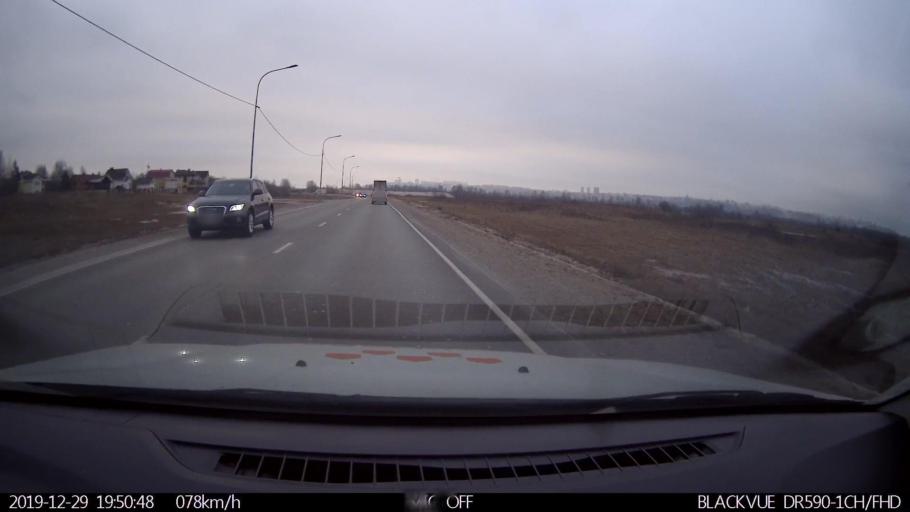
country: RU
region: Nizjnij Novgorod
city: Bor
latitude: 56.3642
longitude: 44.0319
